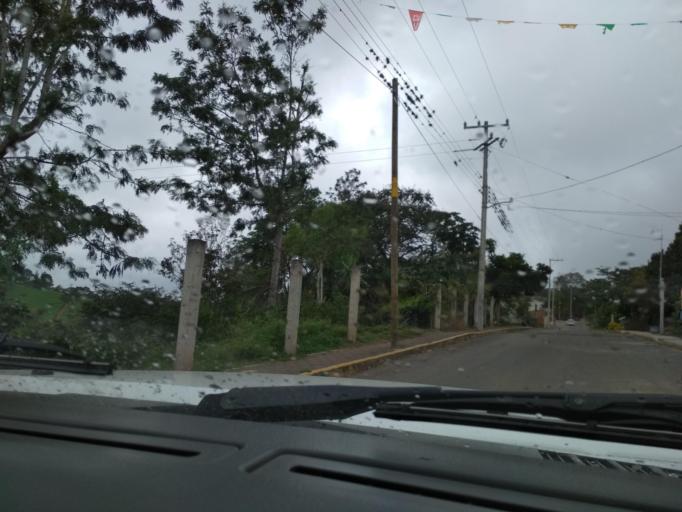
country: MX
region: Veracruz
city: El Castillo
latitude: 19.5396
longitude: -96.8235
